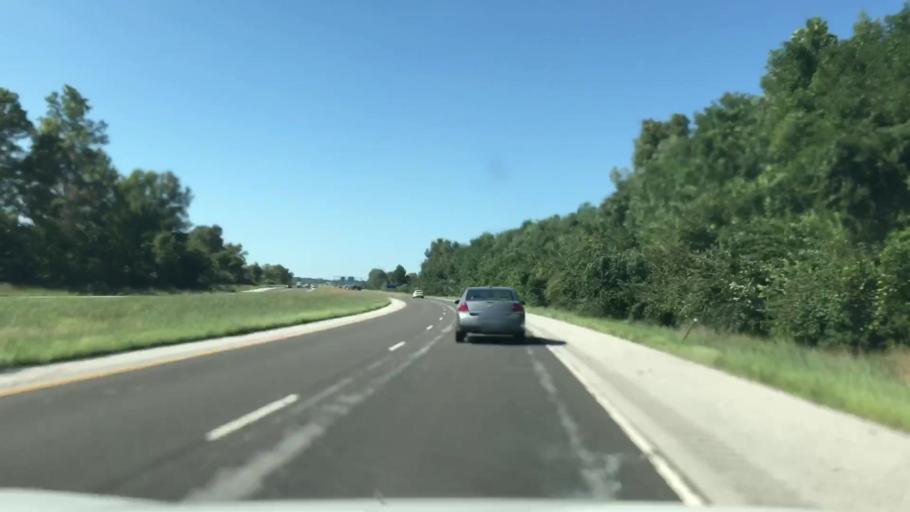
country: US
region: Illinois
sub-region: Madison County
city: South Roxana
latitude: 38.8410
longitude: -90.0441
